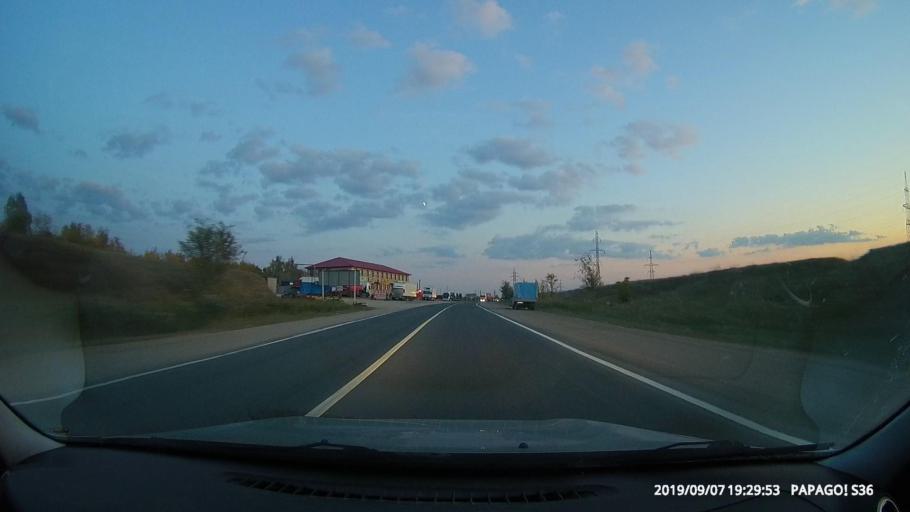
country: RU
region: Samara
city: Chapayevsk
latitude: 52.9975
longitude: 49.7681
